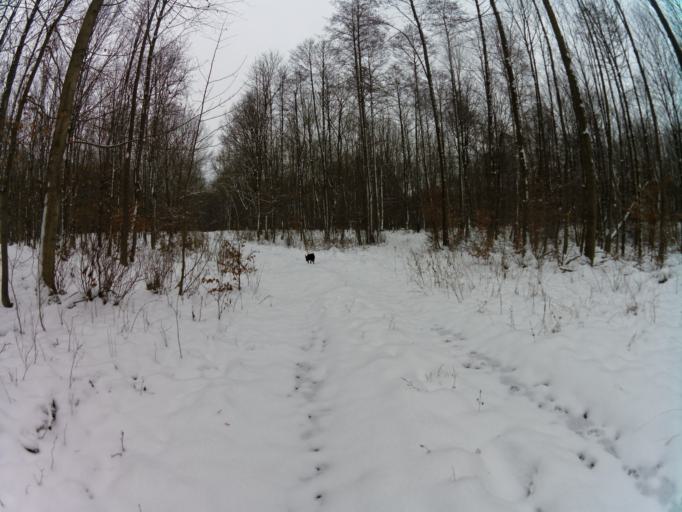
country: PL
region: West Pomeranian Voivodeship
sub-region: Powiat choszczenski
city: Recz
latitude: 53.3288
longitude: 15.5453
